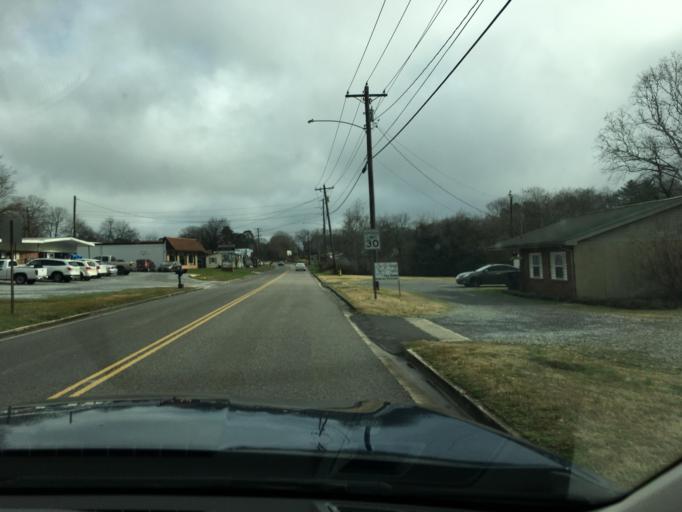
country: US
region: Tennessee
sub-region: McMinn County
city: Athens
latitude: 35.4396
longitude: -84.6219
